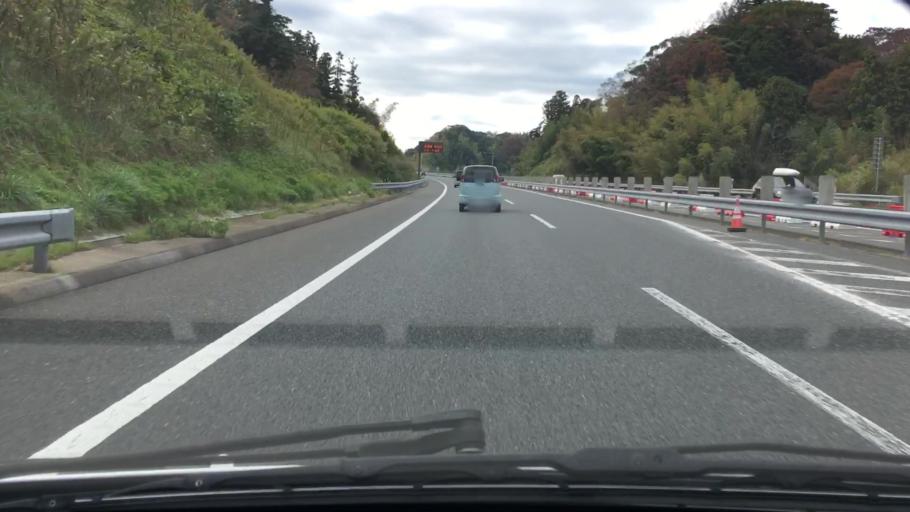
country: JP
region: Chiba
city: Kimitsu
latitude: 35.2586
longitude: 139.8954
